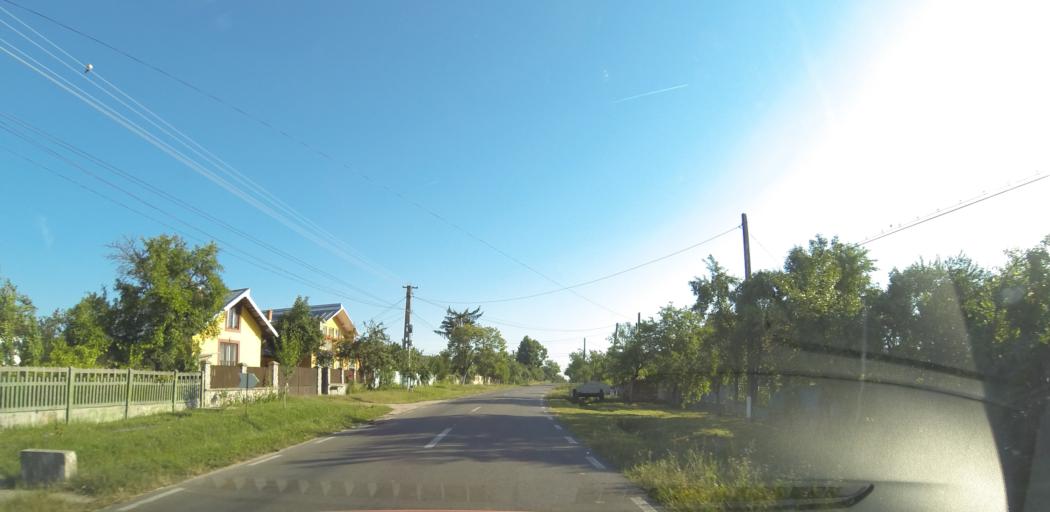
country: RO
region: Valcea
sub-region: Comuna Lacusteni
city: Lacusteni
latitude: 44.6970
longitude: 23.8981
